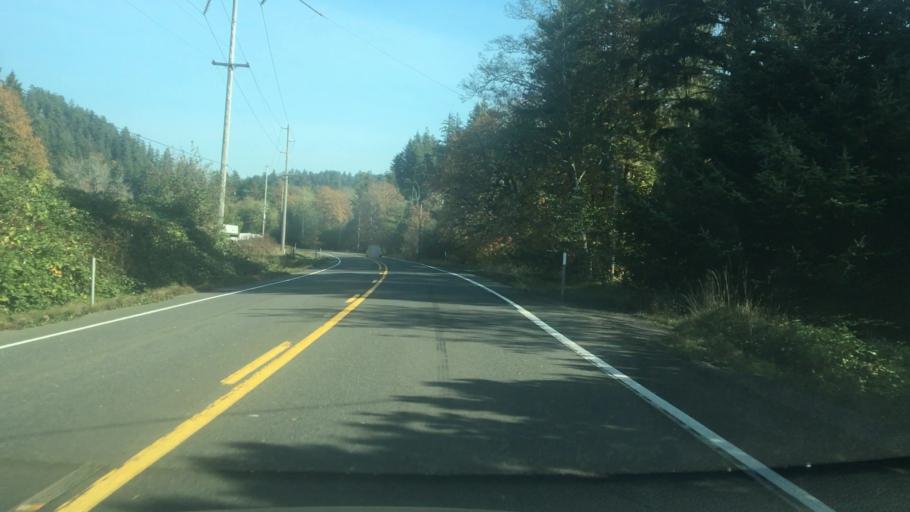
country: US
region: Oregon
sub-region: Lincoln County
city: Rose Lodge
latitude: 45.0225
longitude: -123.8327
